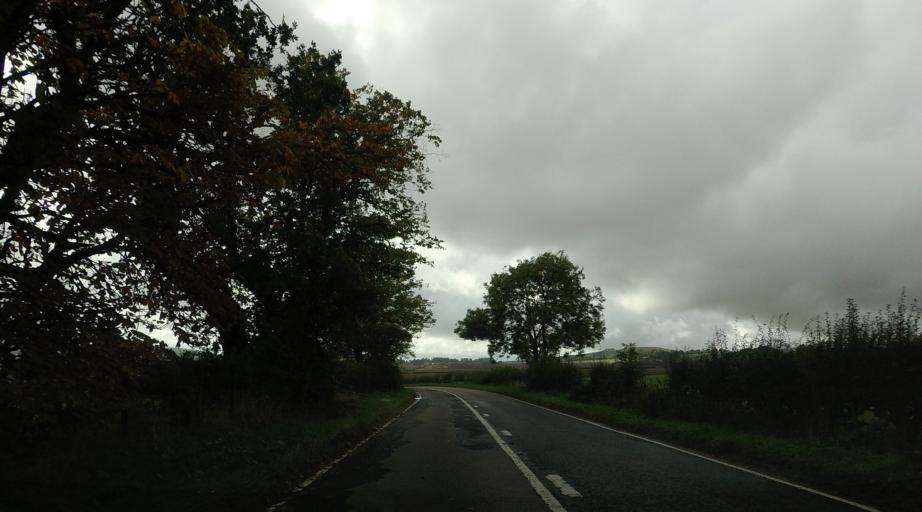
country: GB
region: Scotland
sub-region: Fife
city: Balmullo
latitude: 56.3715
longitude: -2.9312
